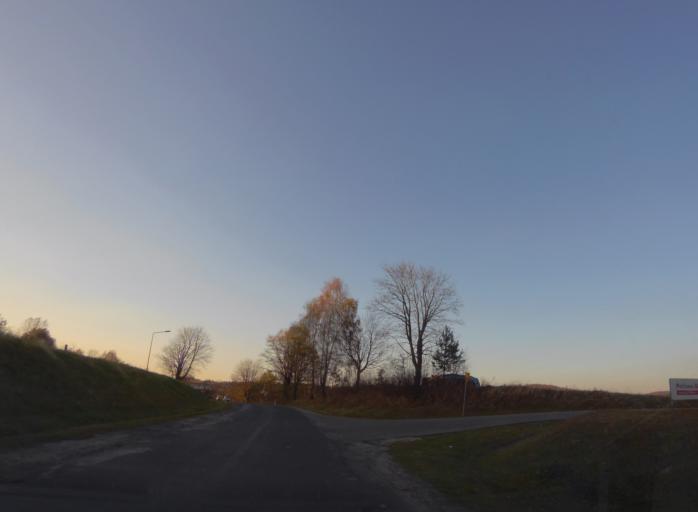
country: PL
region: Subcarpathian Voivodeship
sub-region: Powiat leski
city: Polanczyk
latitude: 49.3770
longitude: 22.4167
